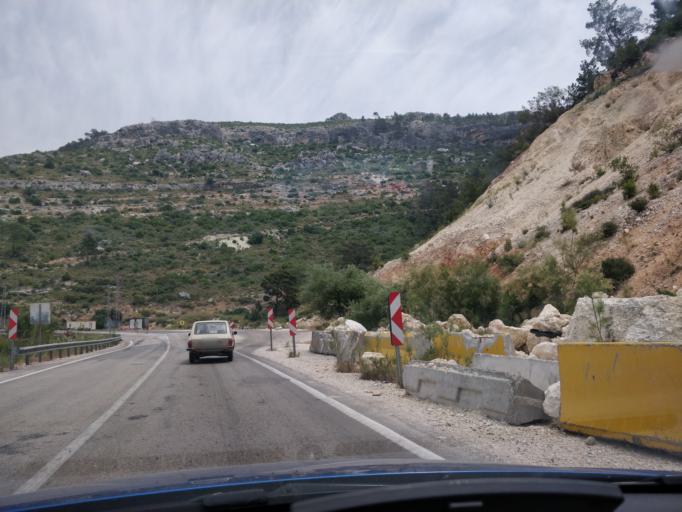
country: TR
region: Mersin
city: Tasucu
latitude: 36.3921
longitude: 33.8385
